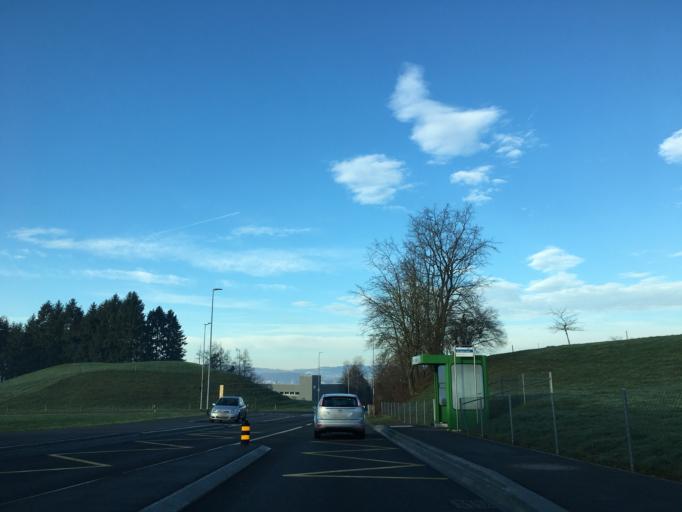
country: CH
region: Lucerne
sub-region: Lucerne-Land District
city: Adligenswil
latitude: 47.0513
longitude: 8.3537
